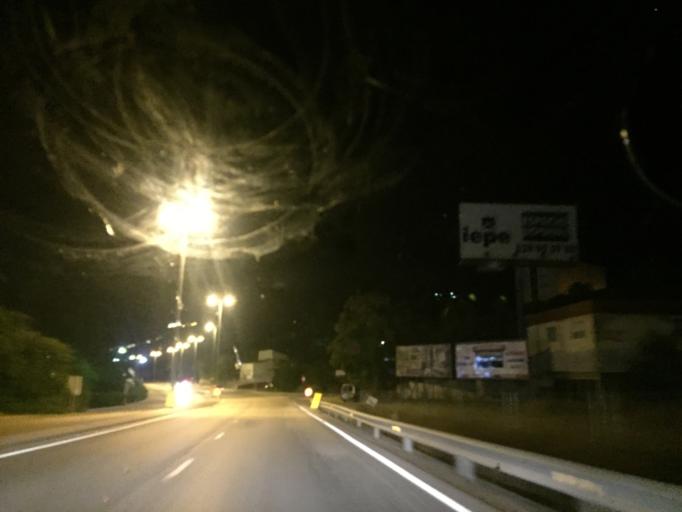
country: ES
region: Andalusia
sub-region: Provincia de Jaen
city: Jaen
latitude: 37.7843
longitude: -3.8269
